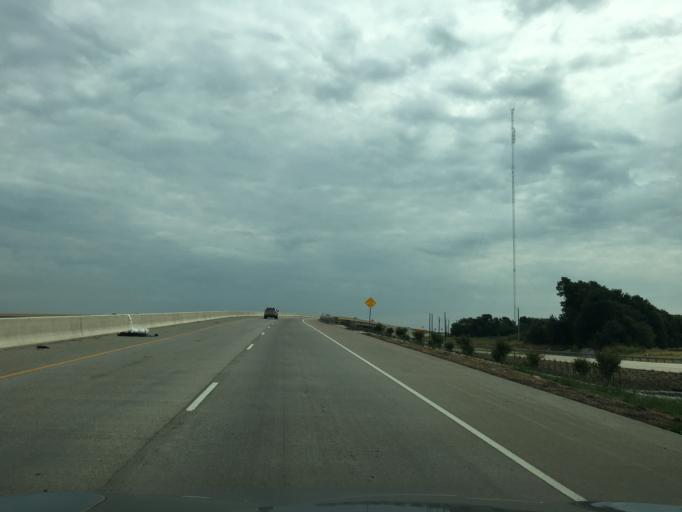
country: US
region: Texas
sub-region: Collin County
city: Melissa
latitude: 33.2629
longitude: -96.6014
